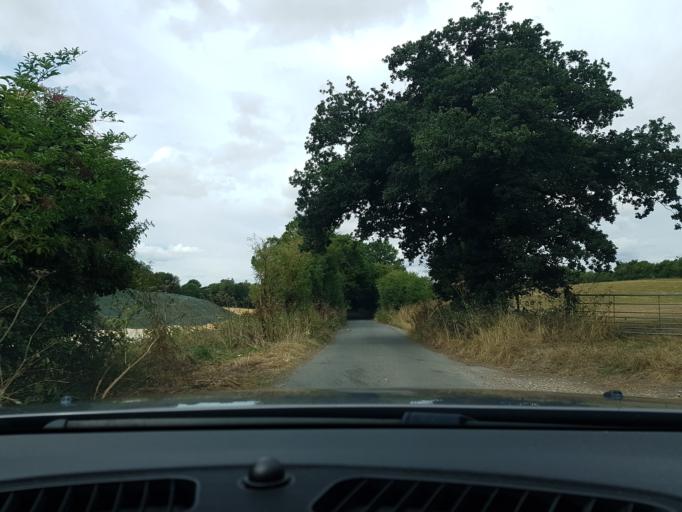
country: GB
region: England
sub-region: West Berkshire
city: Kintbury
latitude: 51.4337
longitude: -1.4759
